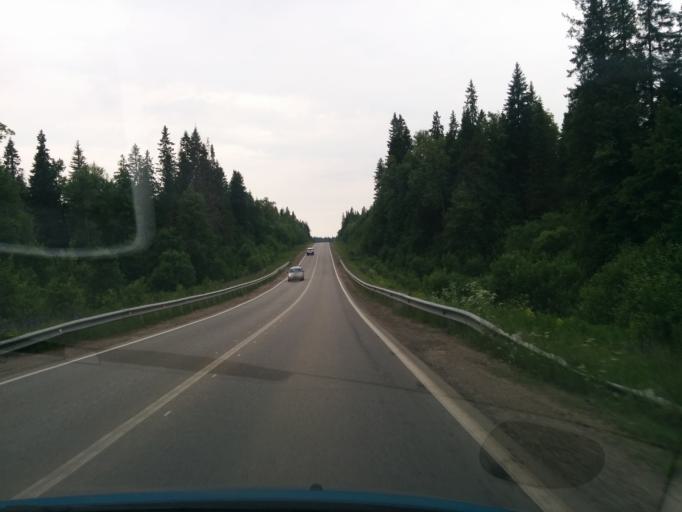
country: RU
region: Perm
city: Perm
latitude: 58.1907
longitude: 56.2152
